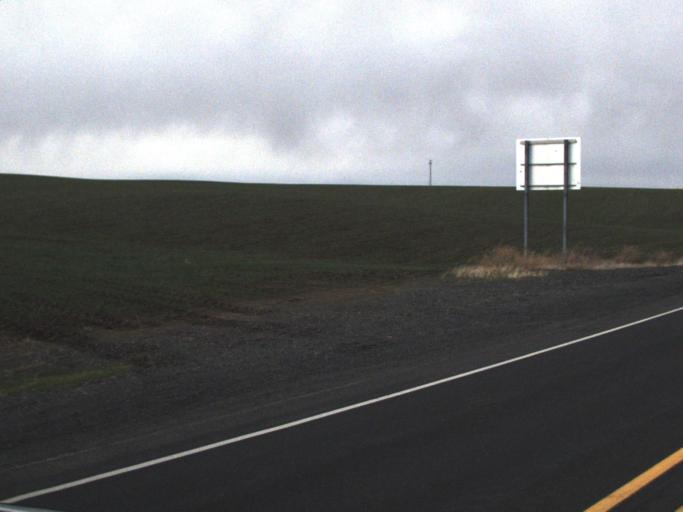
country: US
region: Washington
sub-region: Whitman County
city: Colfax
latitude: 46.8134
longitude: -117.6629
